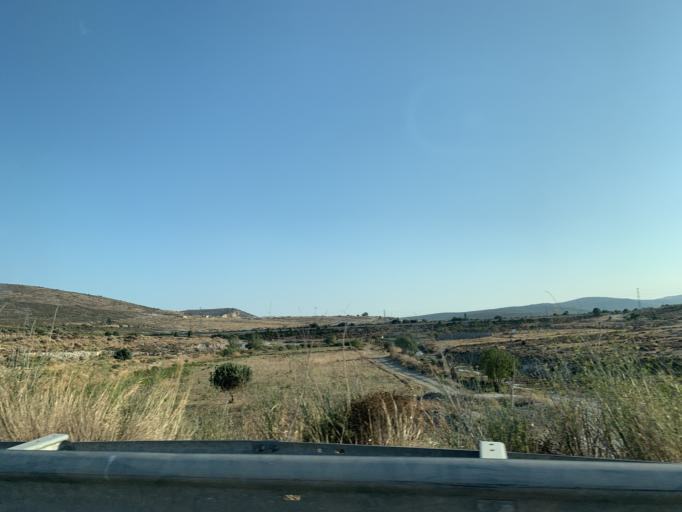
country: TR
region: Izmir
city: Alacati
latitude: 38.2804
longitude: 26.4021
